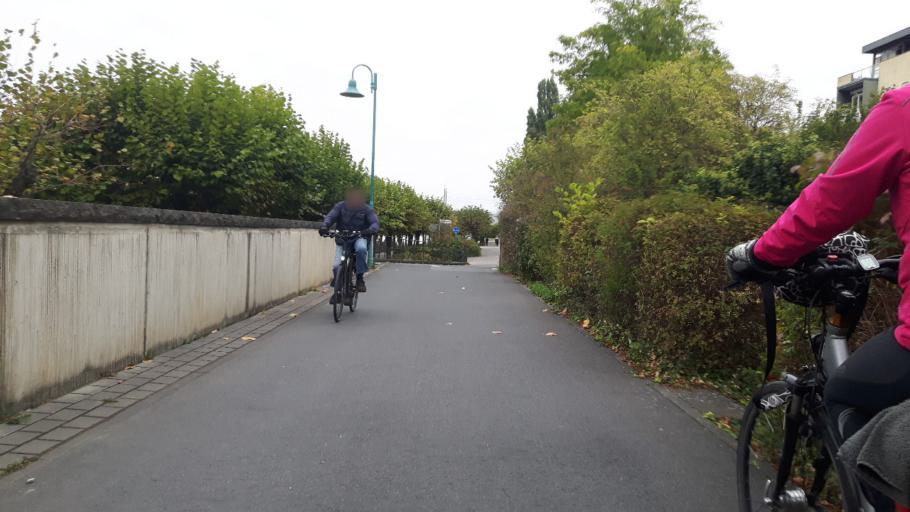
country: DE
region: North Rhine-Westphalia
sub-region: Regierungsbezirk Koln
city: Bonn
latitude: 50.7356
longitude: 7.1141
